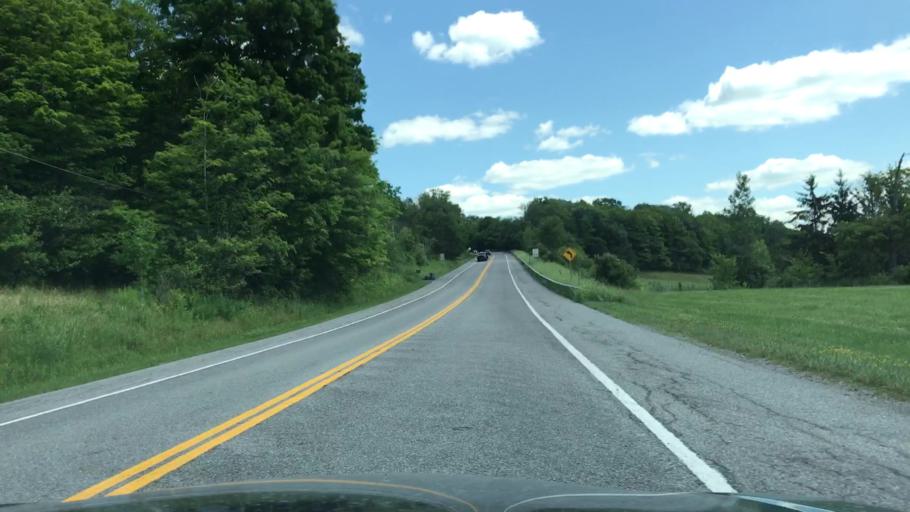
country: US
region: New York
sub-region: Erie County
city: East Aurora
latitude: 42.7662
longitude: -78.5180
